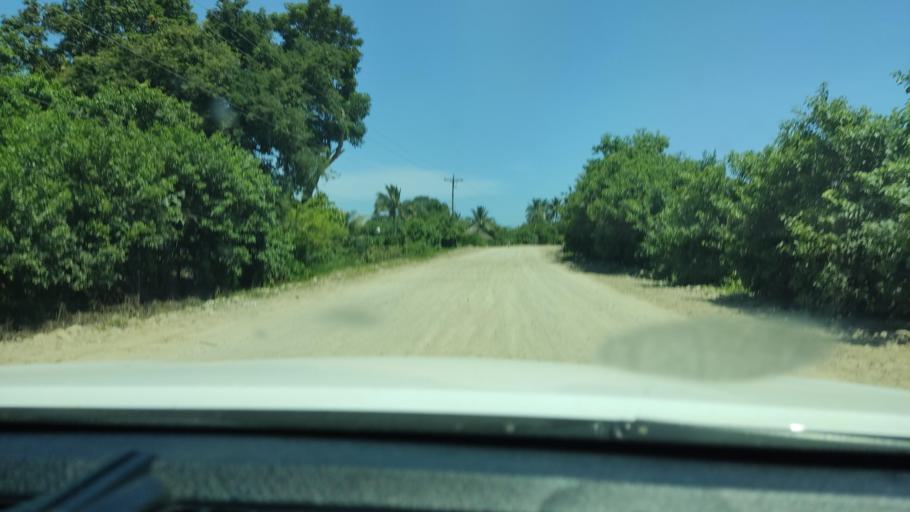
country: SV
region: Ahuachapan
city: San Francisco Menendez
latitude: 13.7755
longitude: -90.1129
